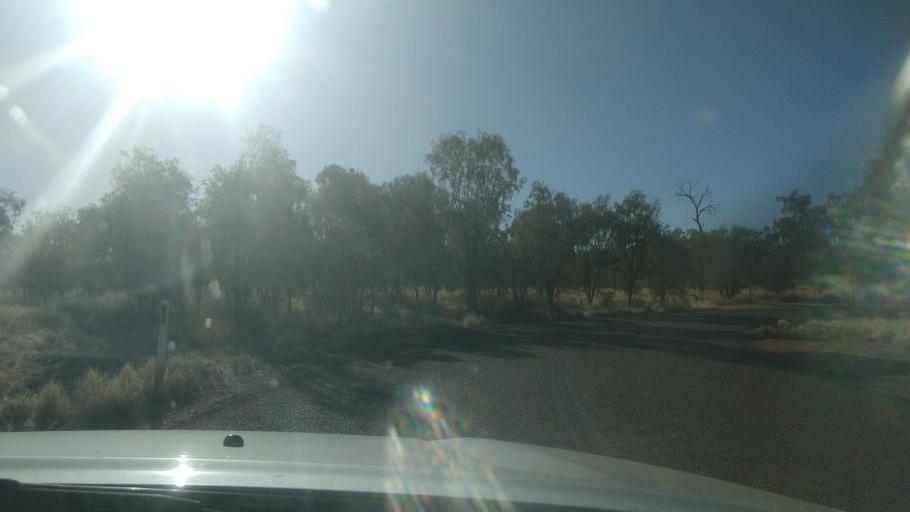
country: AU
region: Northern Territory
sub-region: Alice Springs
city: Alice Springs
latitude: -23.7004
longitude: 133.8279
